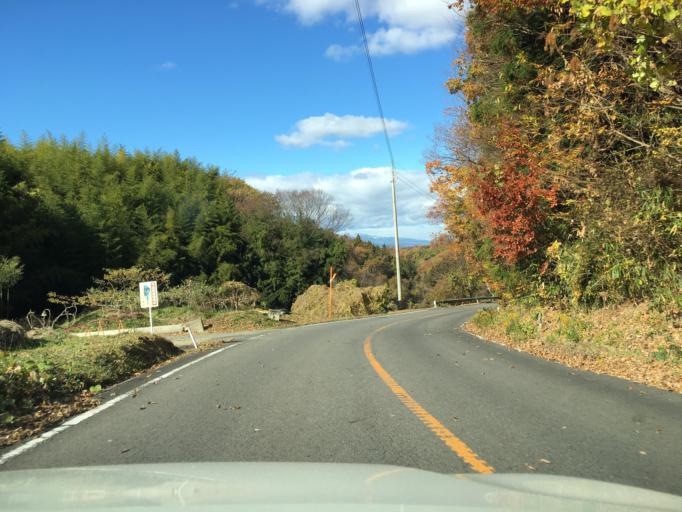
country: JP
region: Fukushima
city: Miharu
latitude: 37.4518
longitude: 140.5069
